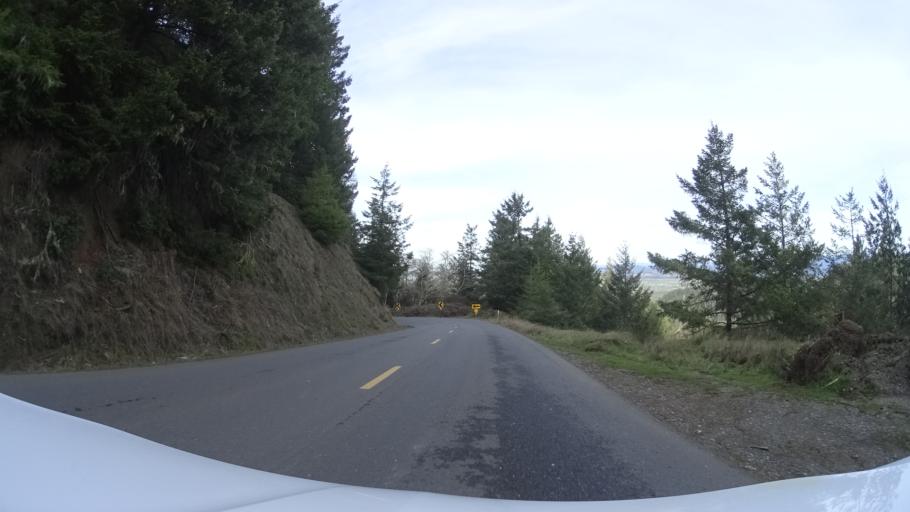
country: US
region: California
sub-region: Humboldt County
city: Ferndale
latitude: 40.5597
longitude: -124.2726
